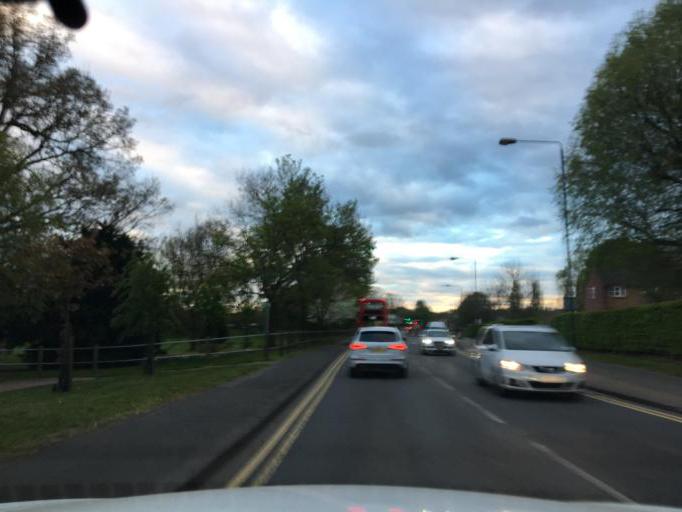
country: GB
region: England
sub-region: Greater London
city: Sidcup
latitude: 51.4218
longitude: 0.0997
